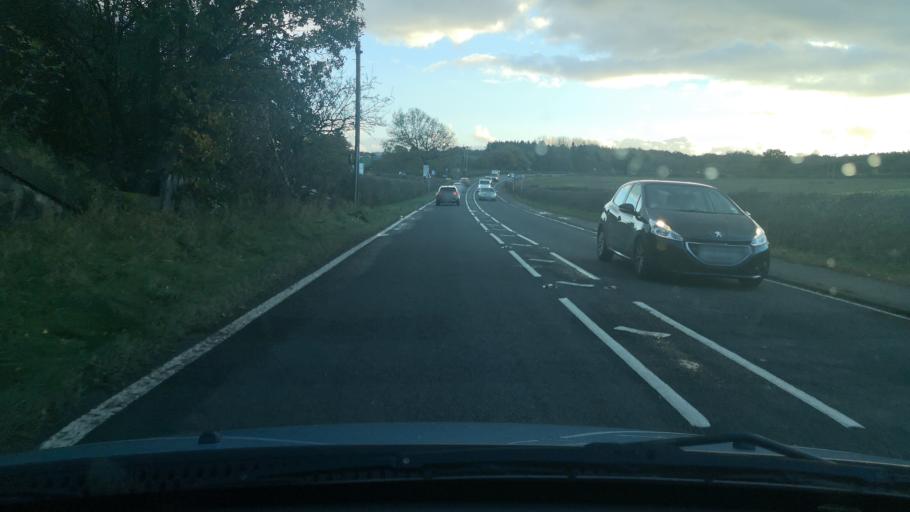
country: GB
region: England
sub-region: City and Borough of Wakefield
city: Crigglestone
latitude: 53.6404
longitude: -1.5474
